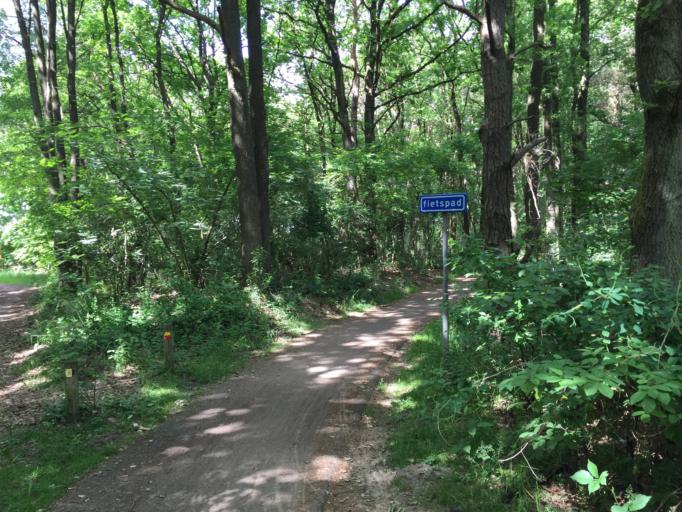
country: NL
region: Drenthe
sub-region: Gemeente De Wolden
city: Ruinen
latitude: 52.7934
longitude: 6.3524
